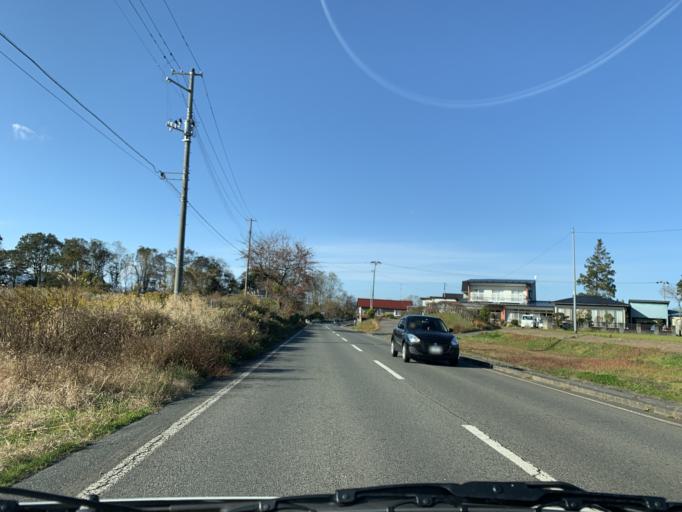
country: JP
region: Iwate
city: Mizusawa
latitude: 39.1832
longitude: 141.1297
